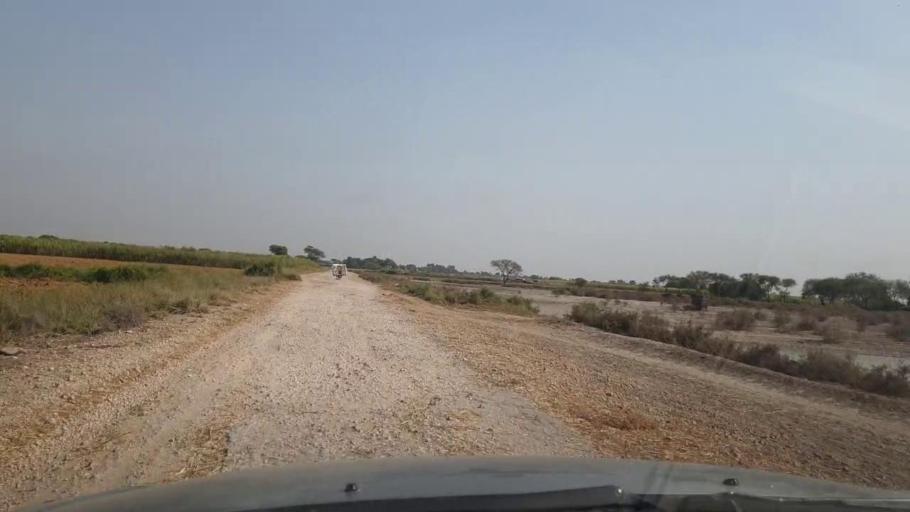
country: PK
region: Sindh
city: Bulri
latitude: 24.9127
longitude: 68.3654
